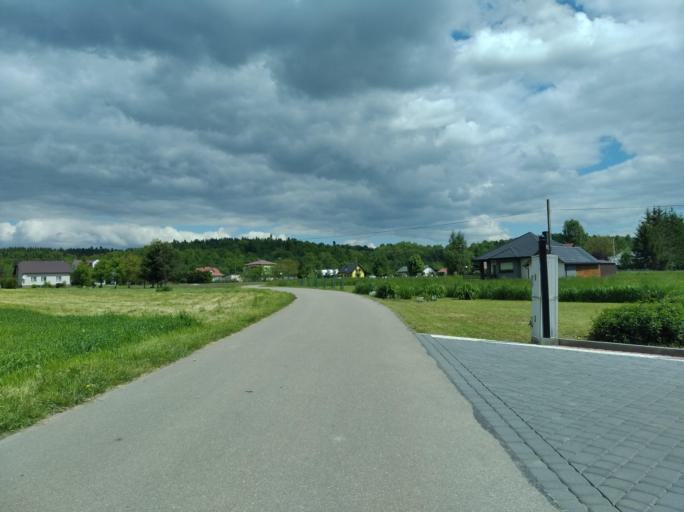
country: PL
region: Subcarpathian Voivodeship
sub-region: Powiat brzozowski
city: Jasionow
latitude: 49.6634
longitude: 21.9894
